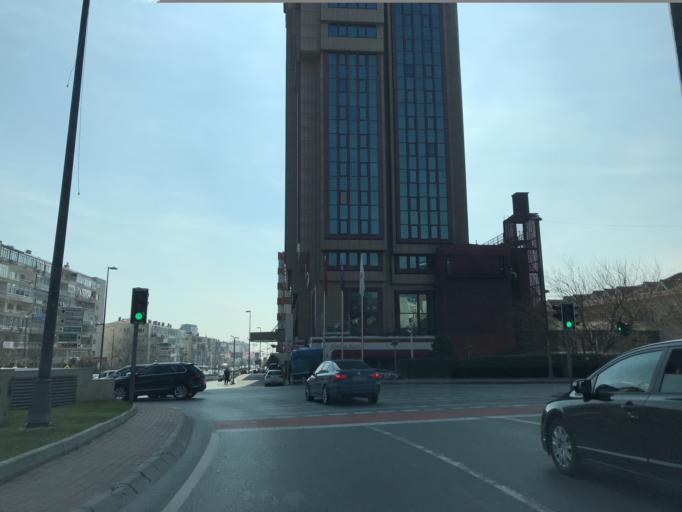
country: TR
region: Istanbul
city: Sisli
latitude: 41.0631
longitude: 29.0116
